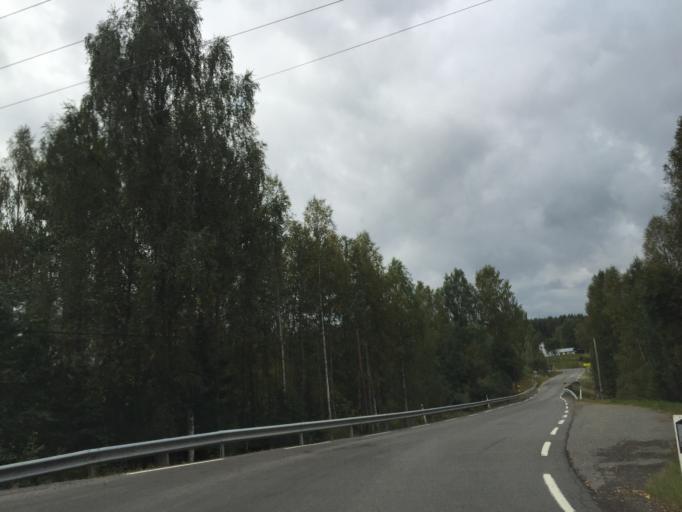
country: NO
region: Hedmark
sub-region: Loten
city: Loten
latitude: 60.6547
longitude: 11.3918
